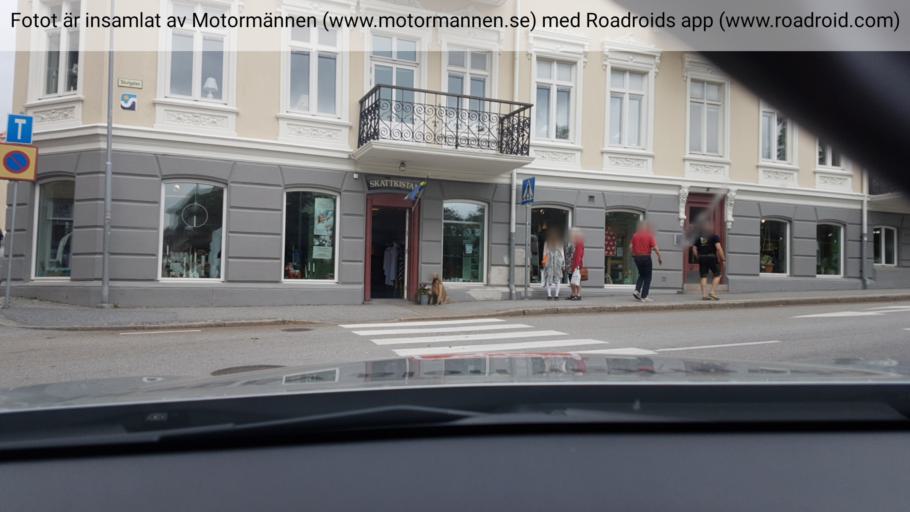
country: SE
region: Vaestra Goetaland
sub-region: Stromstads Kommun
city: Stroemstad
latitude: 58.9380
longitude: 11.1741
